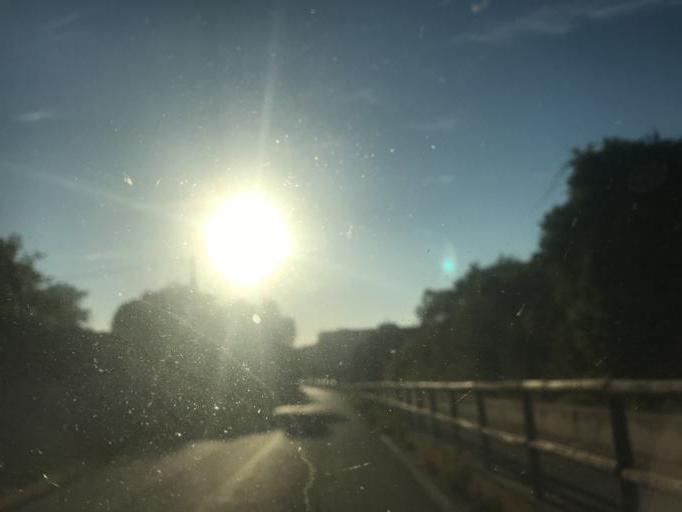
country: IT
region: Sardinia
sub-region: Provincia di Sassari
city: Alghero
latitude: 40.5551
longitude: 8.3317
